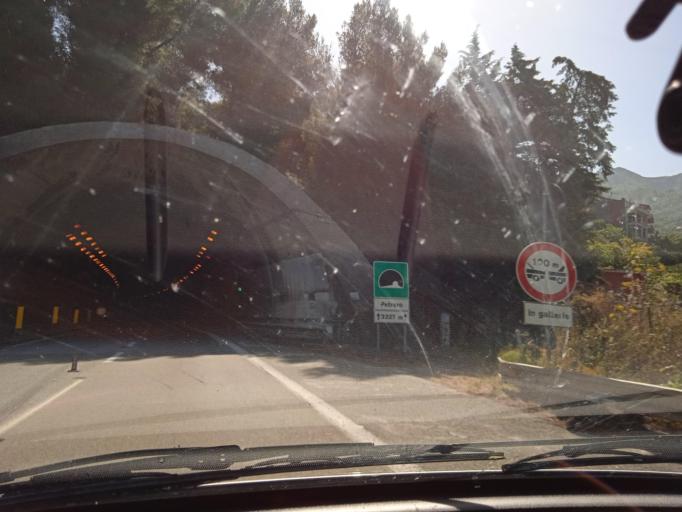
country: IT
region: Sicily
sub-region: Messina
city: Piraino
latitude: 38.1398
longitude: 14.8721
